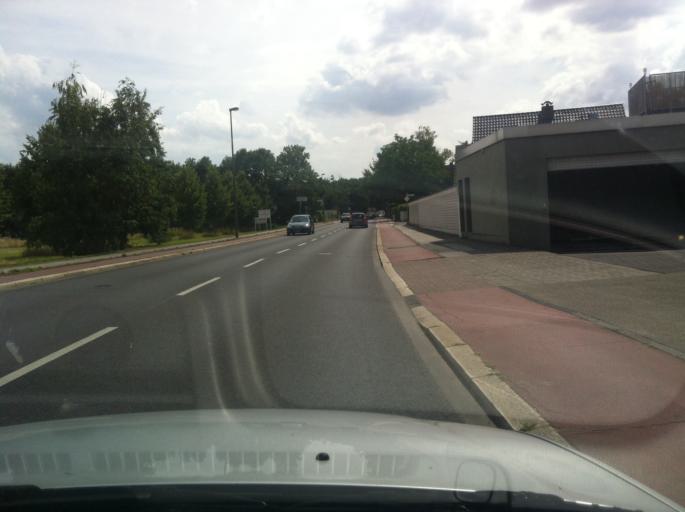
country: DE
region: North Rhine-Westphalia
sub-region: Regierungsbezirk Koln
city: Porz am Rhein
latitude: 50.8729
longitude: 7.0497
